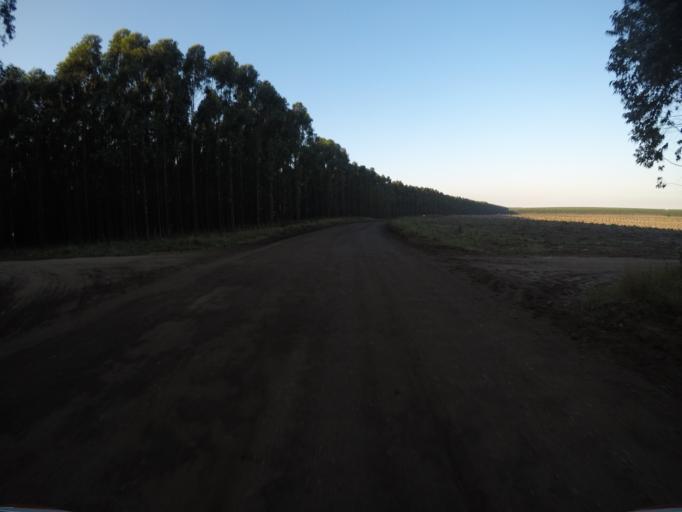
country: ZA
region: KwaZulu-Natal
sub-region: uThungulu District Municipality
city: KwaMbonambi
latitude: -28.6726
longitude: 32.0979
